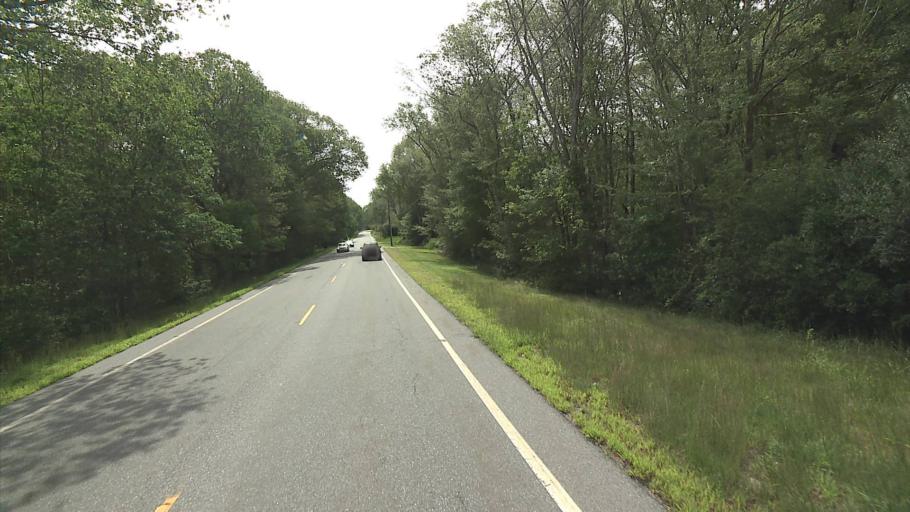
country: US
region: Connecticut
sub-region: Windham County
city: Putnam
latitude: 41.9114
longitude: -71.8697
